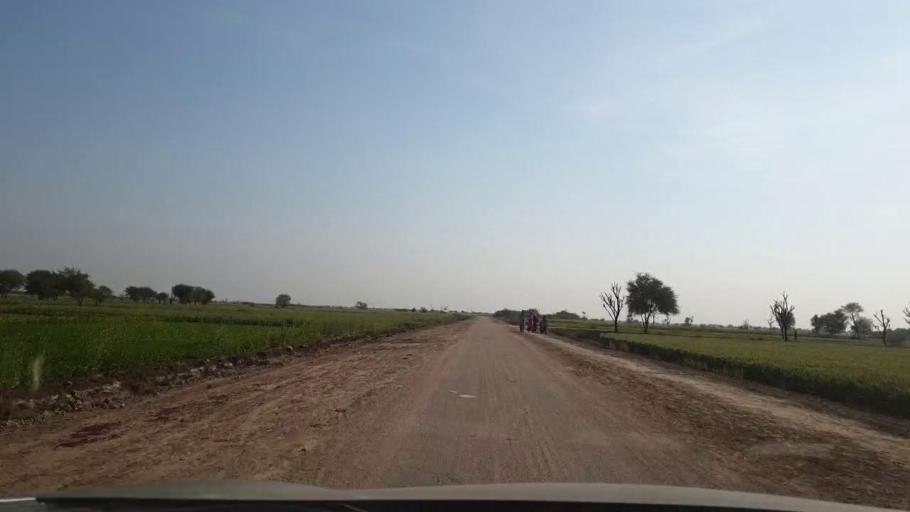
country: PK
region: Sindh
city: Berani
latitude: 25.7166
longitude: 68.8066
